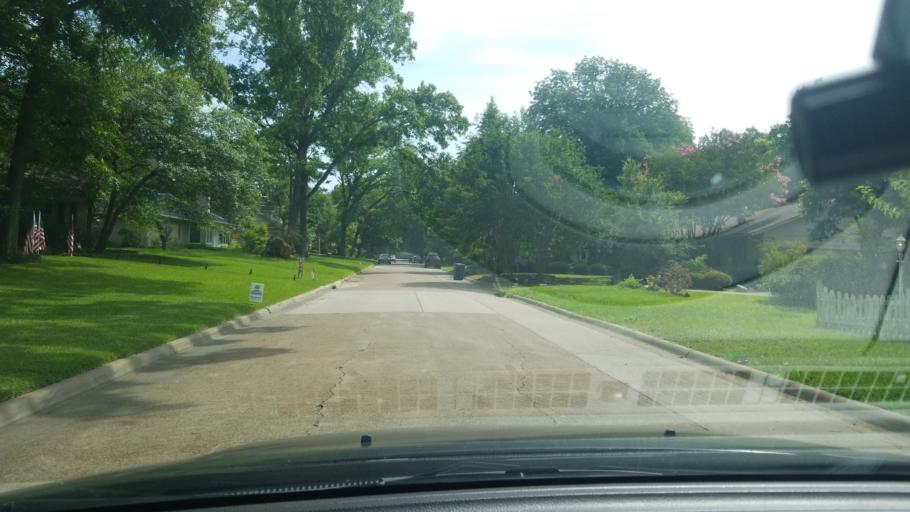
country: US
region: Texas
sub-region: Dallas County
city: Highland Park
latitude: 32.8110
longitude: -96.7125
